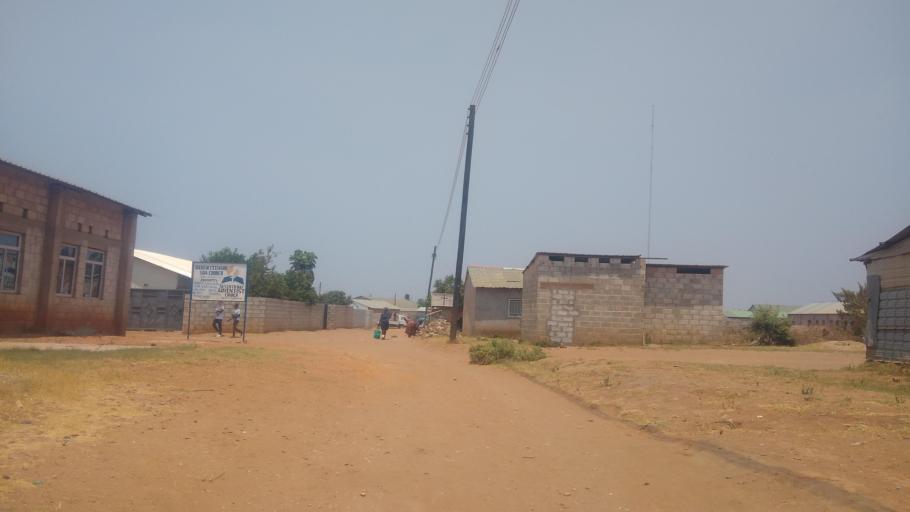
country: ZM
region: Lusaka
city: Lusaka
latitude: -15.4367
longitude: 28.3770
